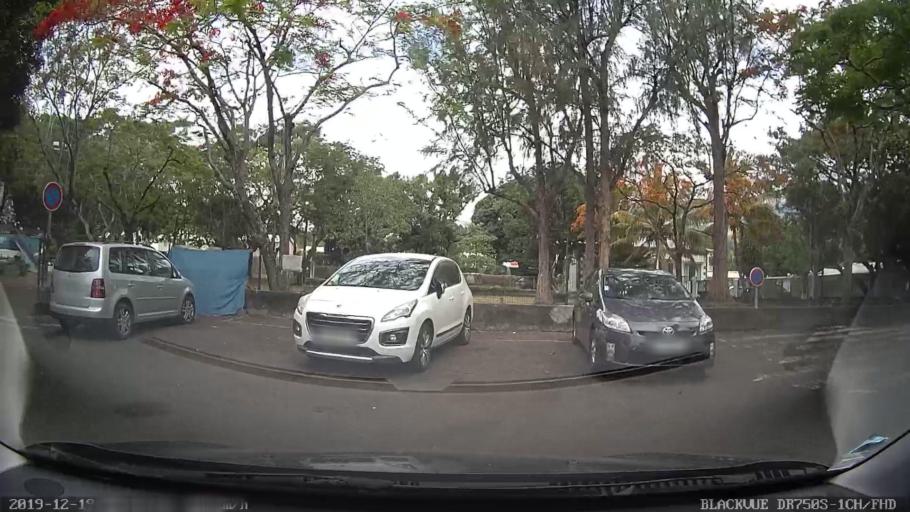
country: RE
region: Reunion
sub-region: Reunion
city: Sainte-Marie
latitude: -20.9135
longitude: 55.5104
